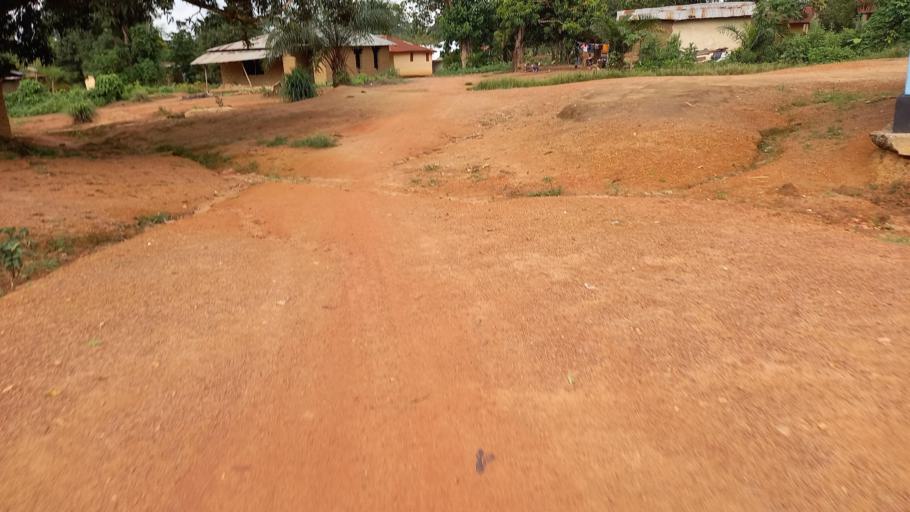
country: SL
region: Eastern Province
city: Kailahun
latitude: 8.2843
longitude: -10.5746
